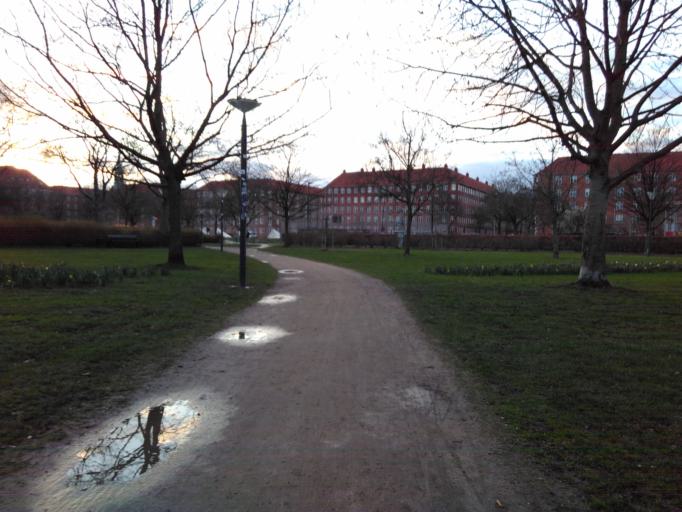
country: DK
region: Capital Region
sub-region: Kobenhavn
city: Christianshavn
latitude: 55.6616
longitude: 12.6187
